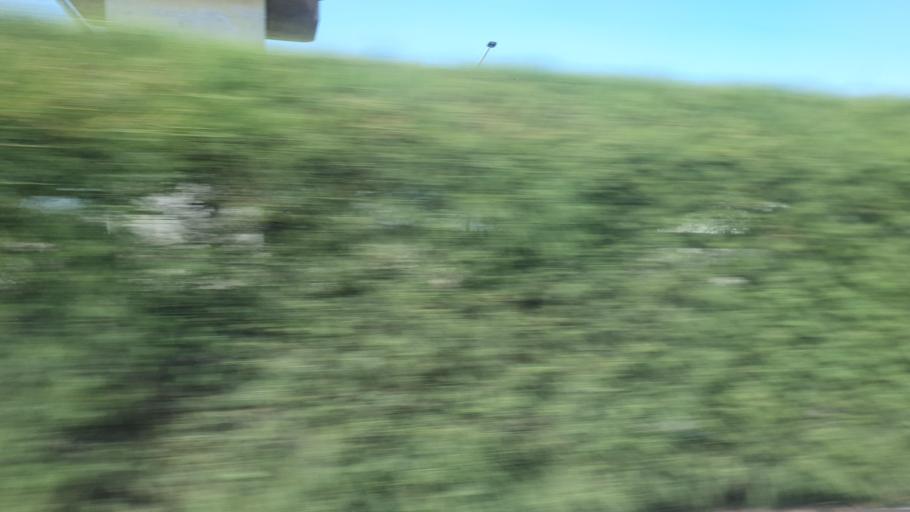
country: TW
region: Taiwan
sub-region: Tainan
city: Tainan
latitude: 23.0090
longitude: 120.2869
